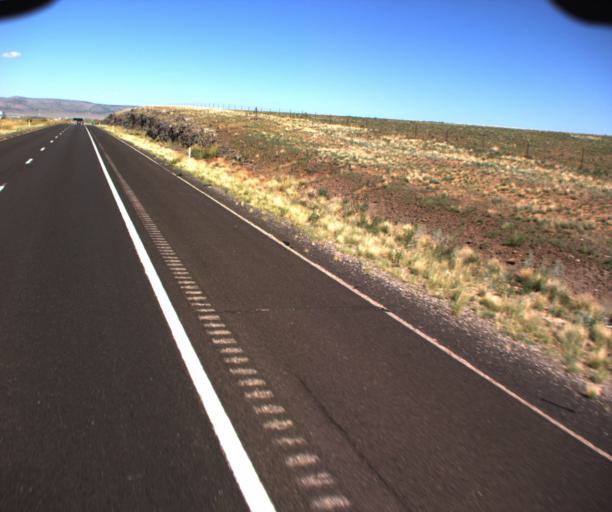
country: US
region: Arizona
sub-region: Yavapai County
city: Paulden
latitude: 35.3017
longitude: -112.8405
